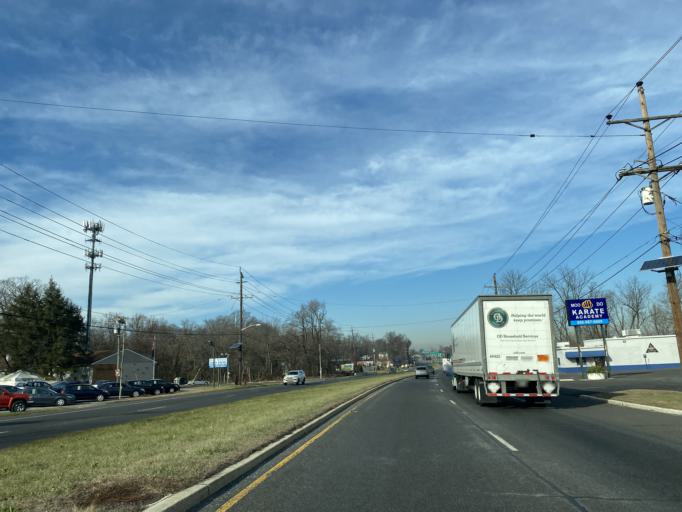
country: US
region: New Jersey
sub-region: Burlington County
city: Maple Shade
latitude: 39.9655
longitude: -75.0005
